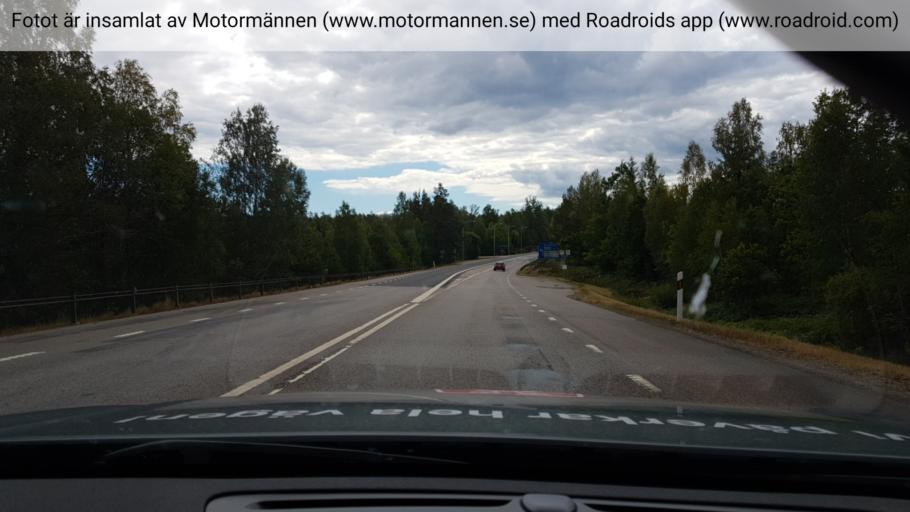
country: SE
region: Kalmar
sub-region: Vasterviks Kommun
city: Ankarsrum
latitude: 57.5910
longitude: 16.4852
